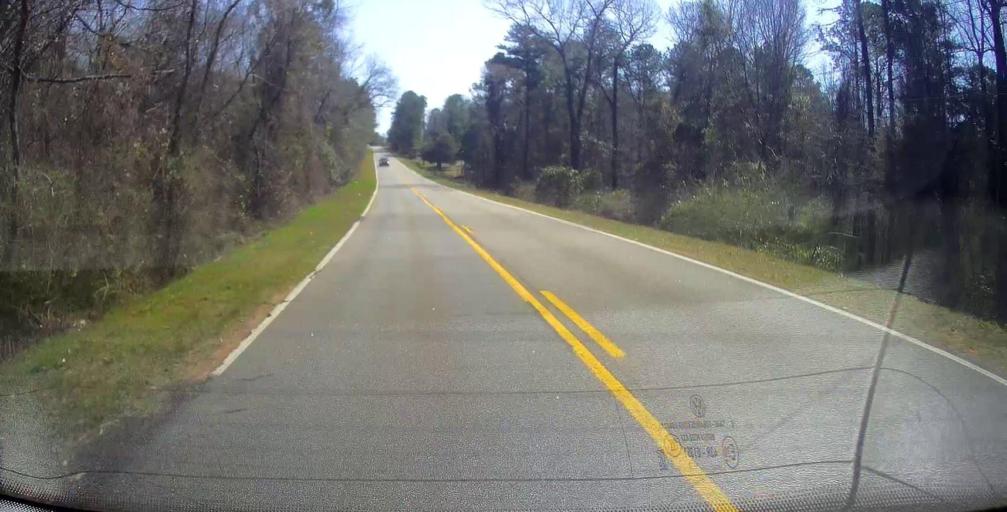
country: US
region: Georgia
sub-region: Peach County
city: Byron
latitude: 32.5818
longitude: -83.7591
